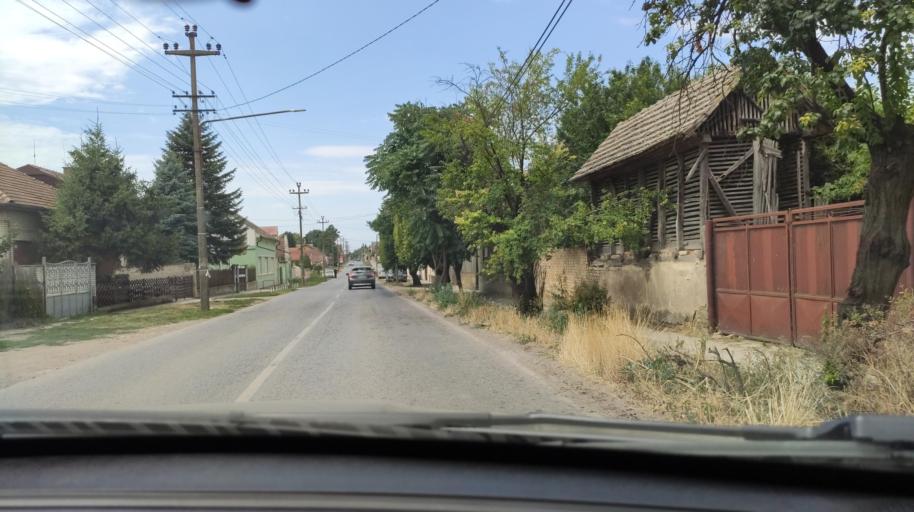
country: RS
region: Autonomna Pokrajina Vojvodina
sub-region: Juznobacki Okrug
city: Temerin
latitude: 45.4136
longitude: 19.8994
